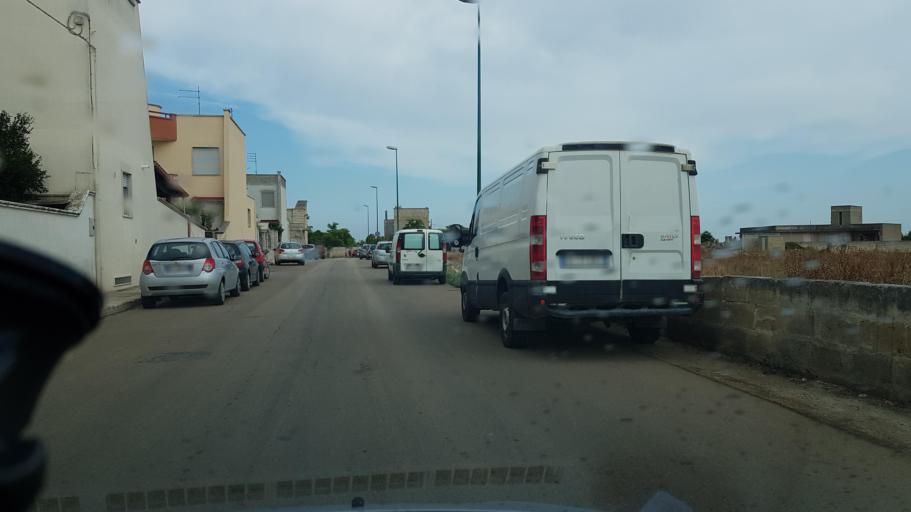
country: IT
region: Apulia
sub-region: Provincia di Brindisi
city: Torre Santa Susanna
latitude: 40.4600
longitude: 17.7441
